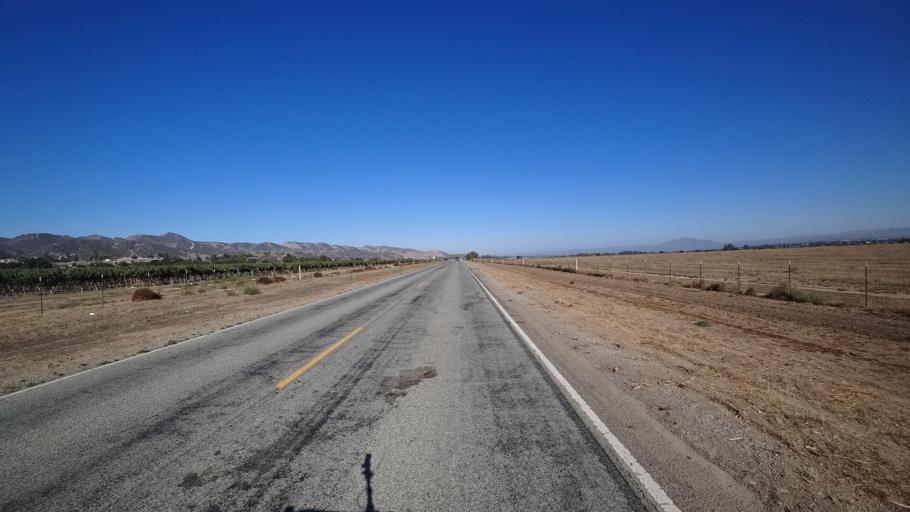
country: US
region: California
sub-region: Monterey County
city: King City
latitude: 36.1856
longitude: -121.1420
